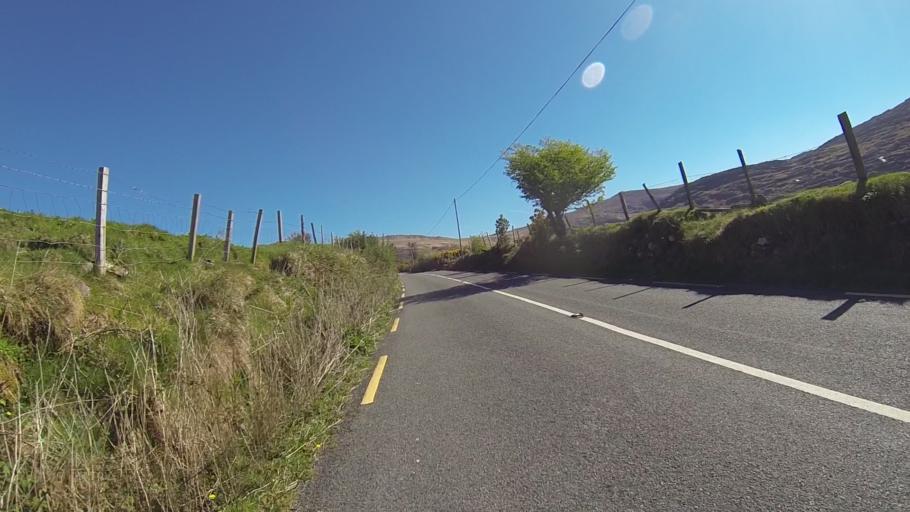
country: IE
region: Munster
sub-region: Ciarrai
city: Kenmare
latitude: 51.7753
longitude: -9.7313
